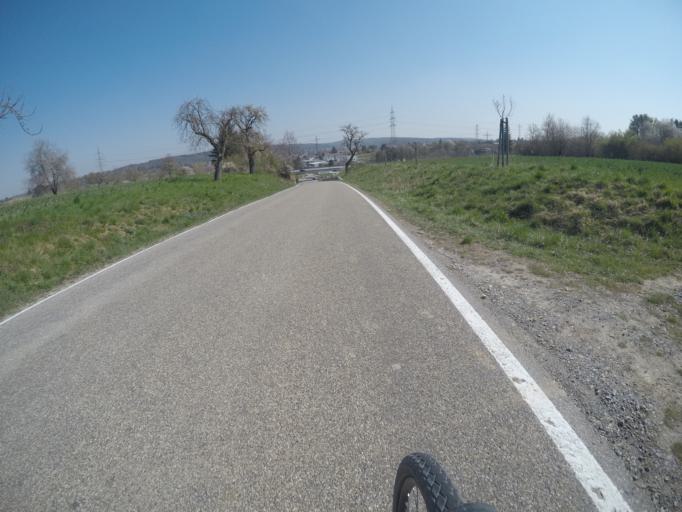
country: DE
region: Baden-Wuerttemberg
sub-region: Regierungsbezirk Stuttgart
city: Magstadt
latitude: 48.7446
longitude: 8.9459
